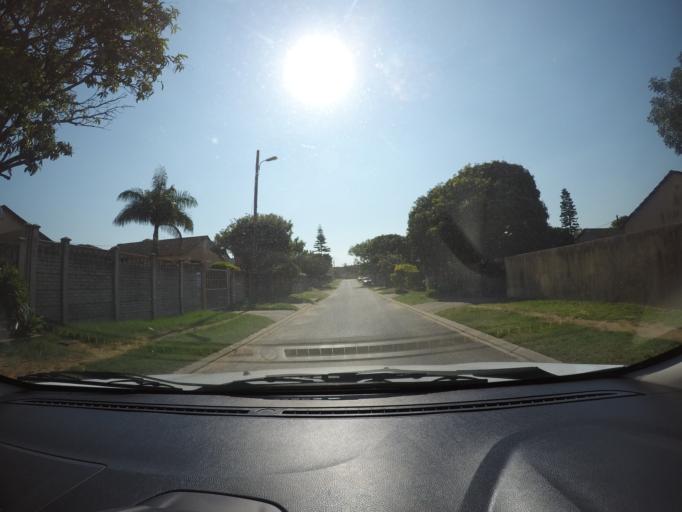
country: ZA
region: KwaZulu-Natal
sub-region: uThungulu District Municipality
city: Richards Bay
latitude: -28.7202
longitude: 32.0446
